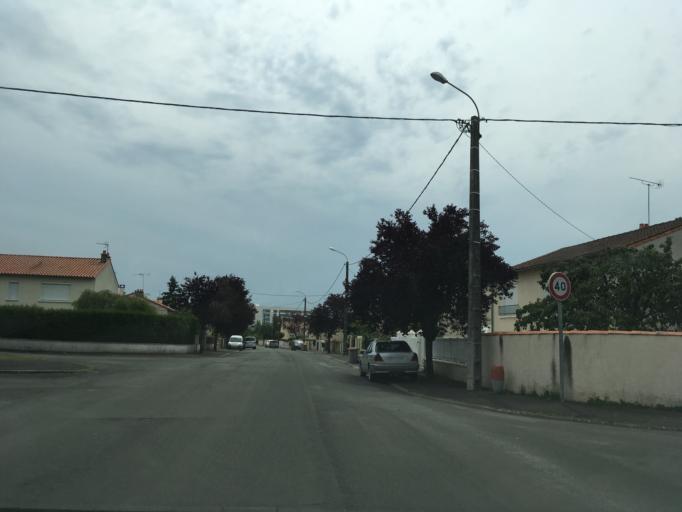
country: FR
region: Poitou-Charentes
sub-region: Departement des Deux-Sevres
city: Niort
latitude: 46.3096
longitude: -0.4755
